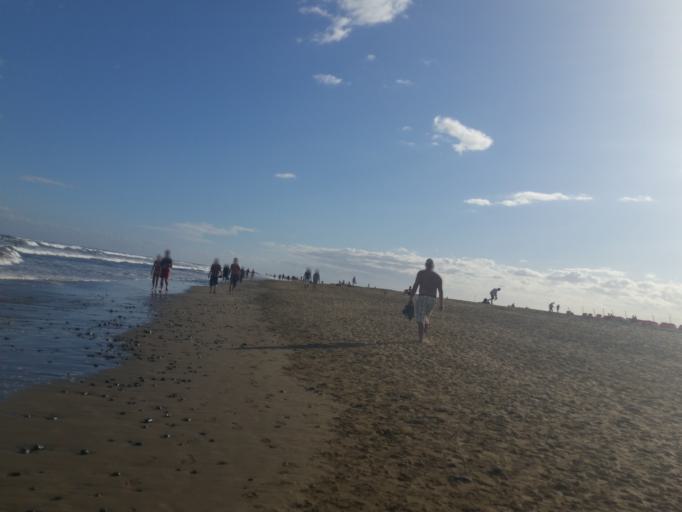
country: ES
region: Canary Islands
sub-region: Provincia de Las Palmas
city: Playa del Ingles
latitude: 27.7439
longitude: -15.5683
